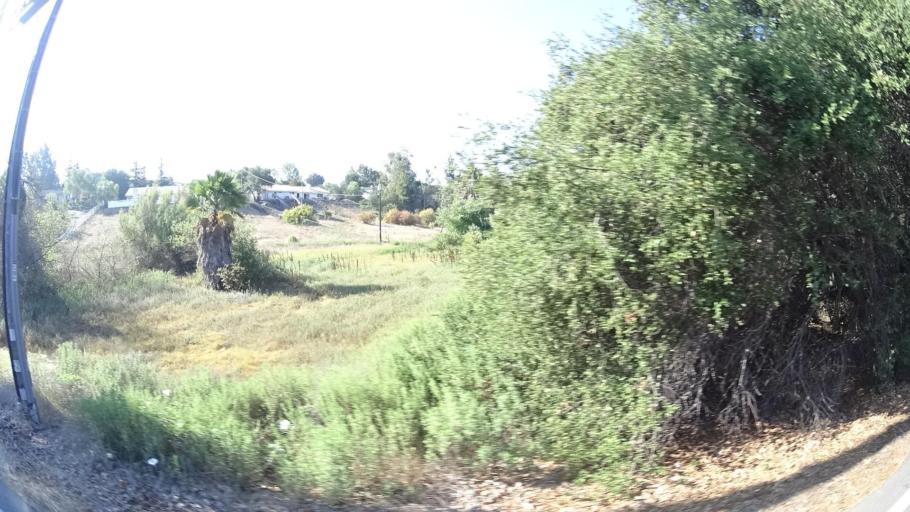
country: US
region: California
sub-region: San Diego County
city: Bonsall
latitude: 33.3218
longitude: -117.2484
